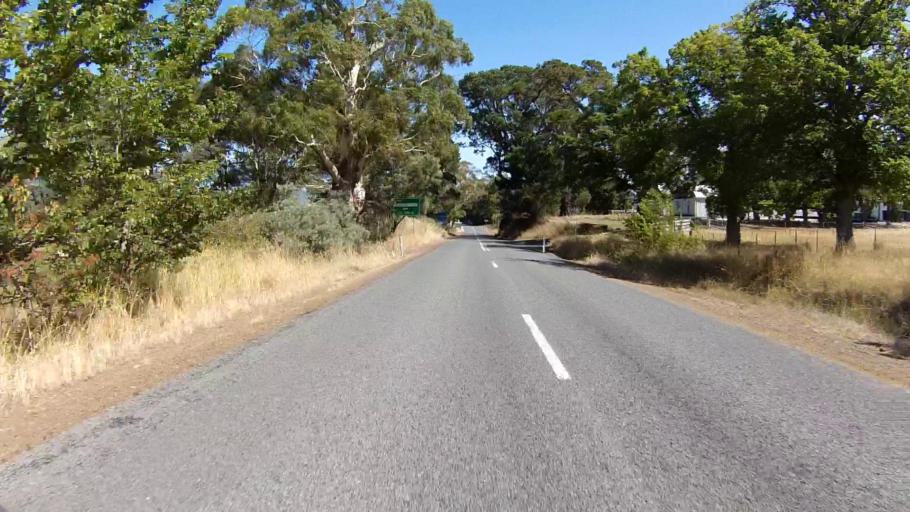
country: AU
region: Tasmania
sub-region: Sorell
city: Sorell
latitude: -42.4957
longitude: 147.9248
